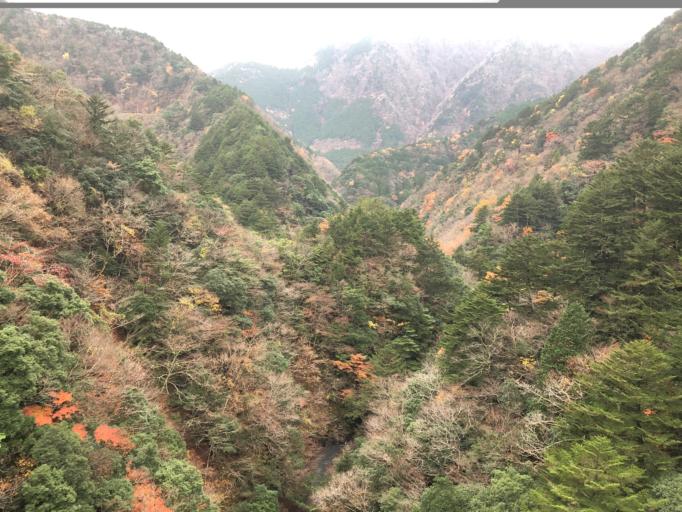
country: JP
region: Shizuoka
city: Shizuoka-shi
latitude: 35.1982
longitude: 138.1831
